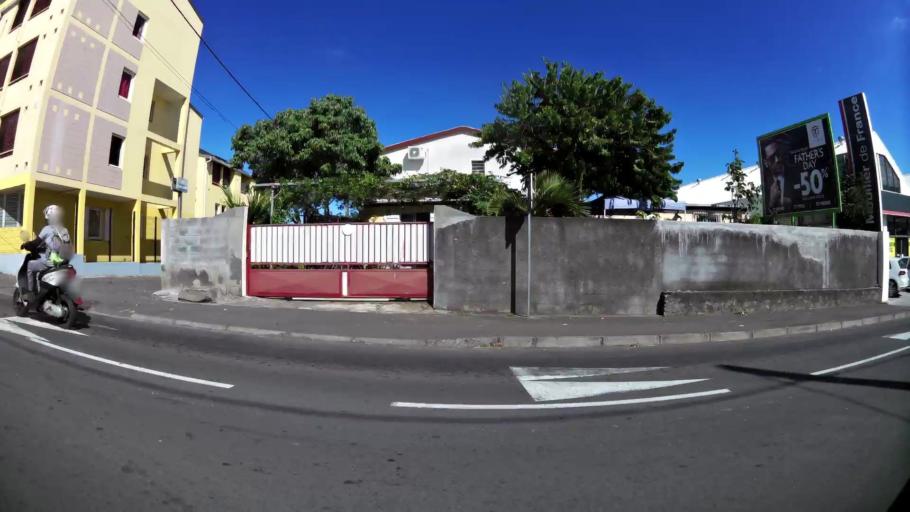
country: RE
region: Reunion
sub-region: Reunion
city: Saint-Pierre
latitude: -21.3345
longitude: 55.4628
